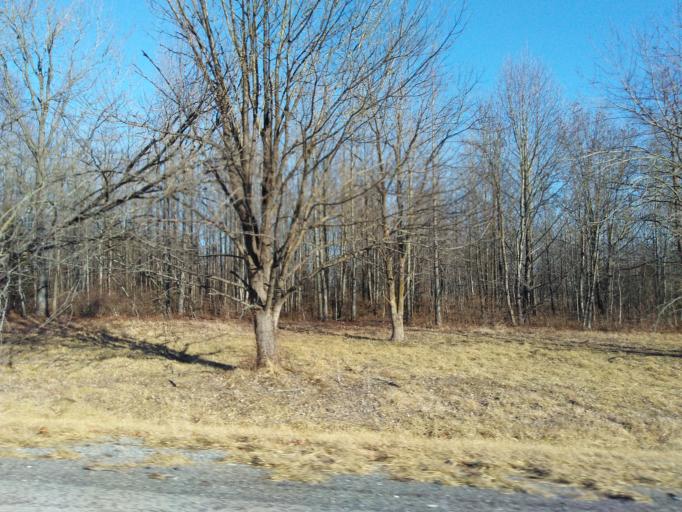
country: US
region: Illinois
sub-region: Franklin County
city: Benton
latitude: 37.9485
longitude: -88.9358
